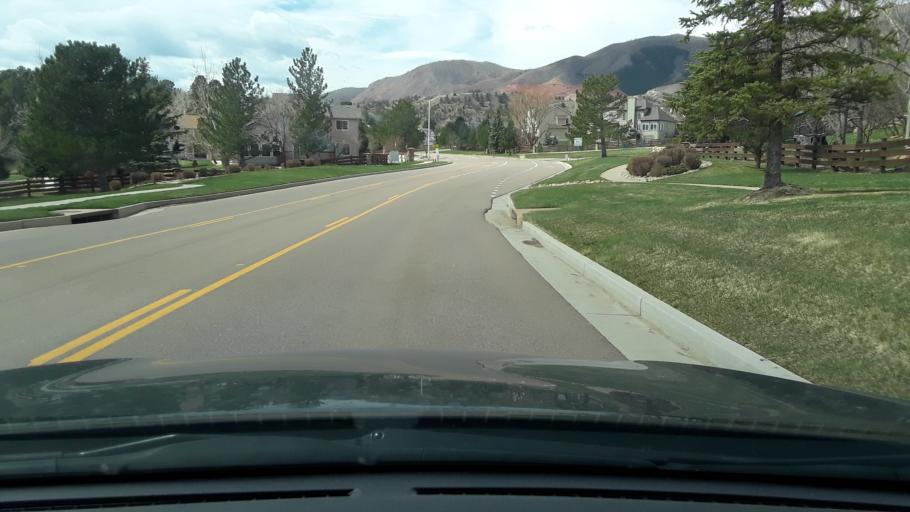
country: US
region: Colorado
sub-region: El Paso County
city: Air Force Academy
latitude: 38.9512
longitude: -104.8641
